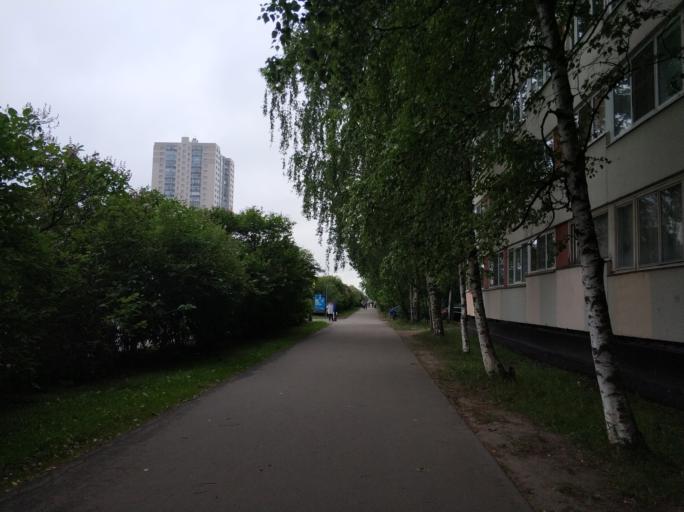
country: RU
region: St.-Petersburg
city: Grazhdanka
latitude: 60.0336
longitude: 30.4087
